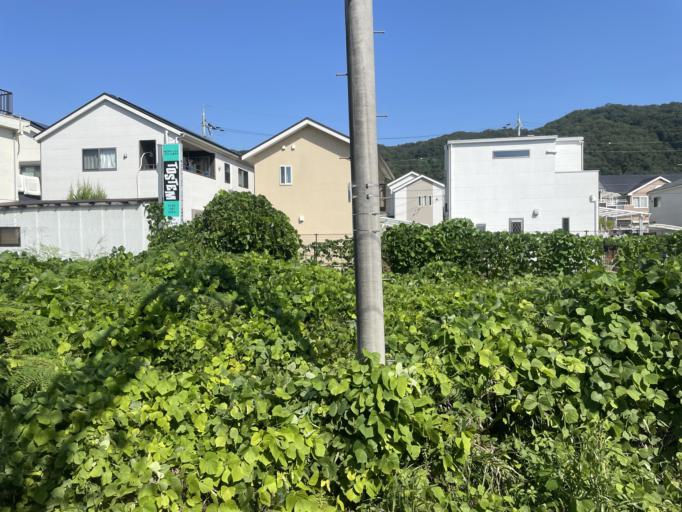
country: JP
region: Nara
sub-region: Ikoma-shi
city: Ikoma
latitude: 34.6284
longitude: 135.7050
